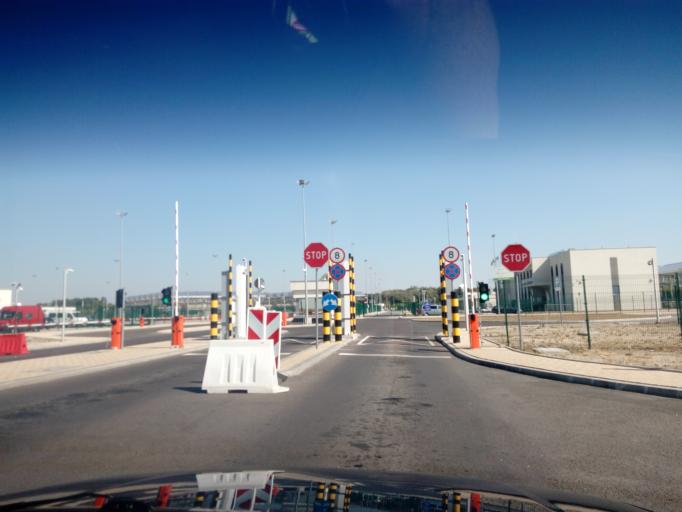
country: PL
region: Lublin Voivodeship
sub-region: Powiat hrubieszowski
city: Horodlo
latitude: 50.8595
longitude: 24.1331
